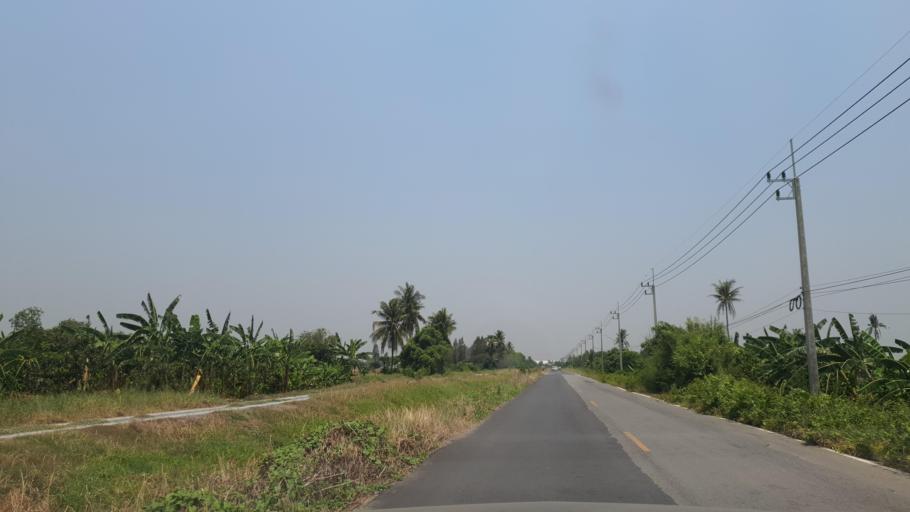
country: TH
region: Suphan Buri
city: Si Prachan
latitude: 14.5903
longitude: 100.1056
